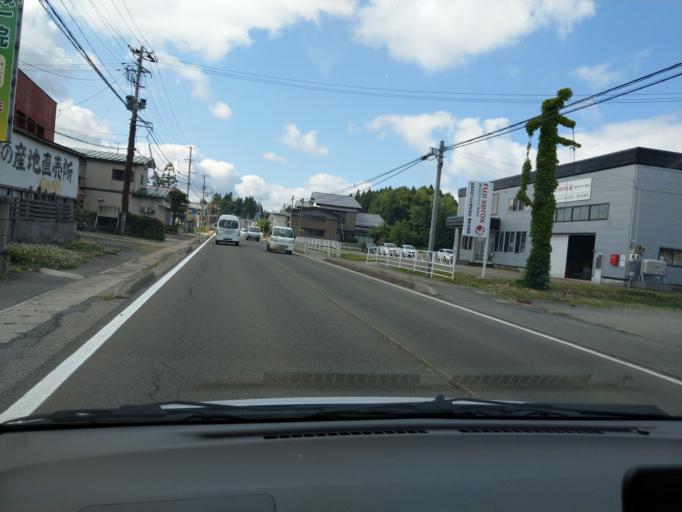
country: JP
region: Akita
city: Yokotemachi
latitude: 39.2797
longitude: 140.5584
